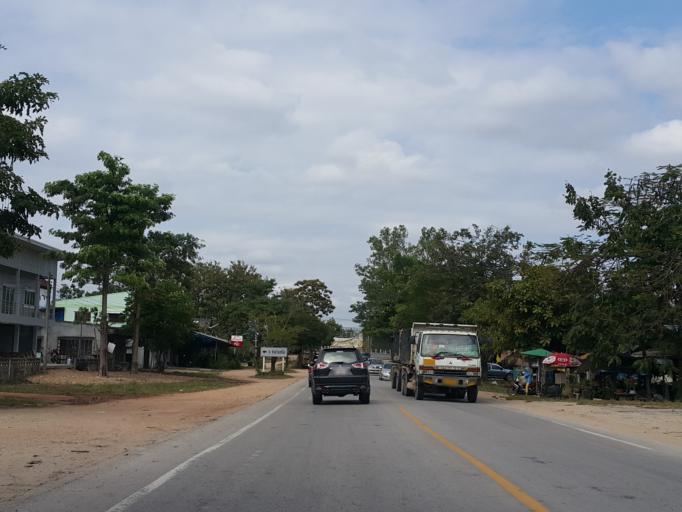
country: TH
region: Lampang
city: Lampang
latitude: 18.3651
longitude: 99.4577
